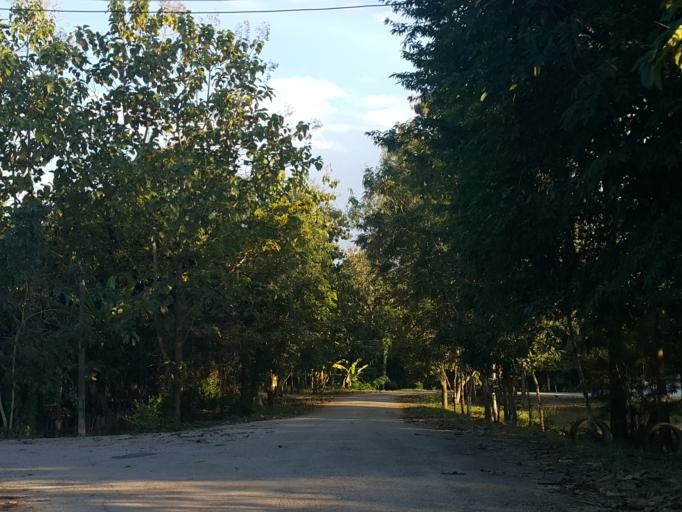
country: TH
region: Lampang
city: Lampang
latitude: 18.4205
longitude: 99.5534
